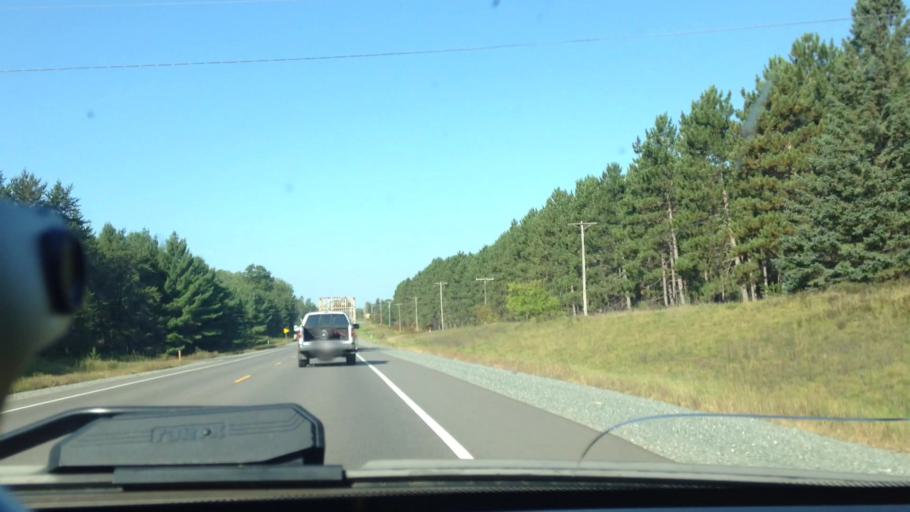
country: US
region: Michigan
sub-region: Dickinson County
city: Iron Mountain
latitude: 45.8760
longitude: -88.1009
